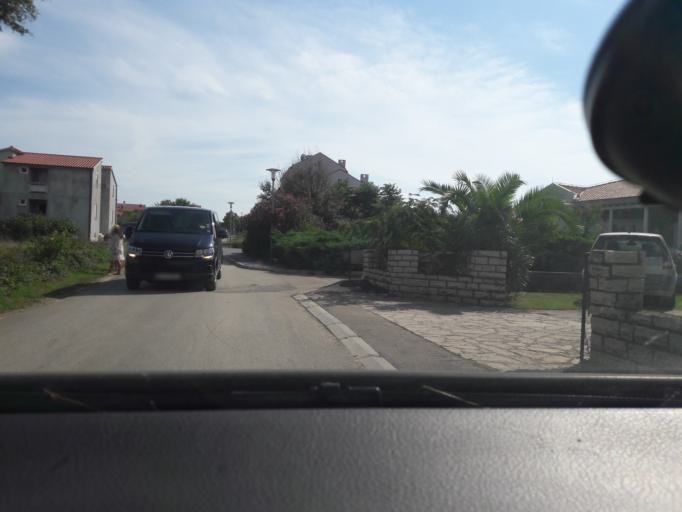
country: HR
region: Zadarska
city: Nin
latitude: 44.2442
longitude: 15.1741
